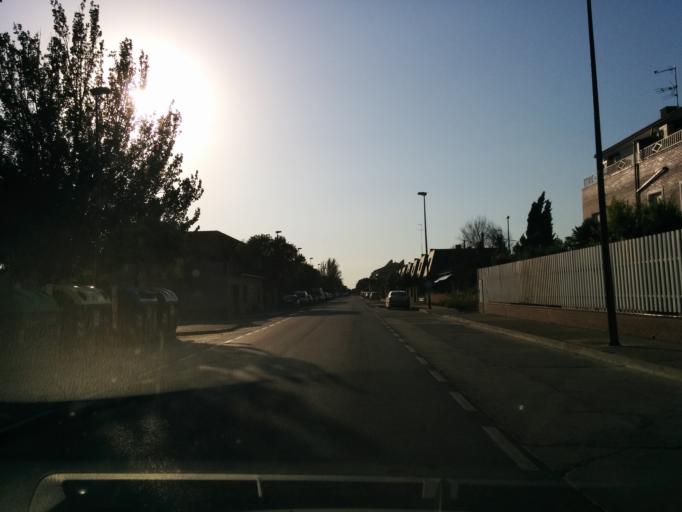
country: ES
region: Aragon
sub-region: Provincia de Zaragoza
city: Zaragoza
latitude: 41.6526
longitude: -0.8297
